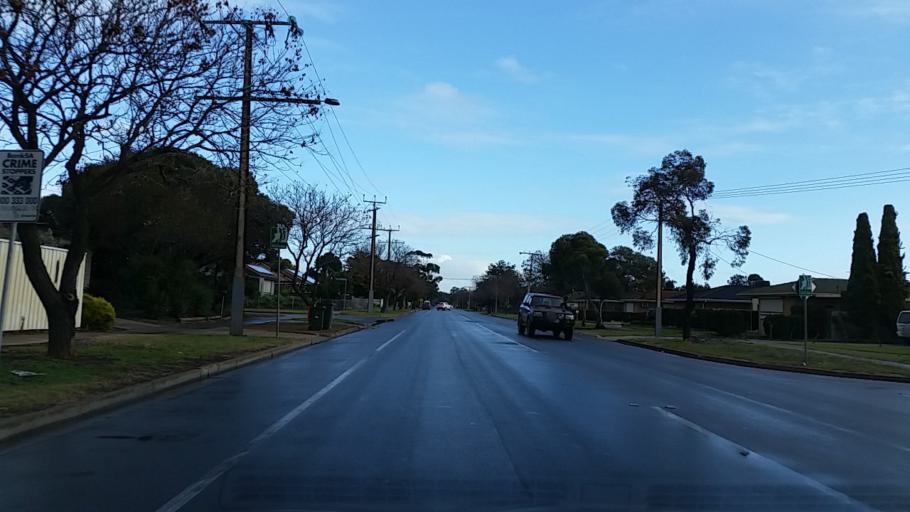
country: AU
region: South Australia
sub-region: Playford
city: Smithfield
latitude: -34.6842
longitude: 138.6786
